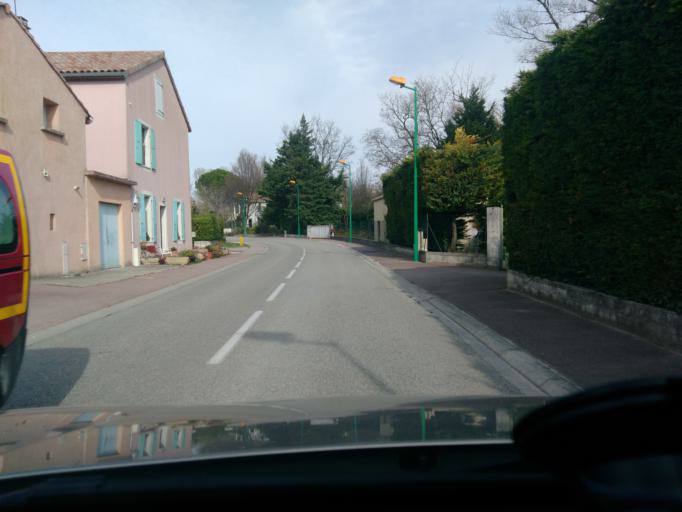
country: FR
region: Rhone-Alpes
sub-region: Departement de l'Ardeche
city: Cruas
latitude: 44.6541
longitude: 4.7744
